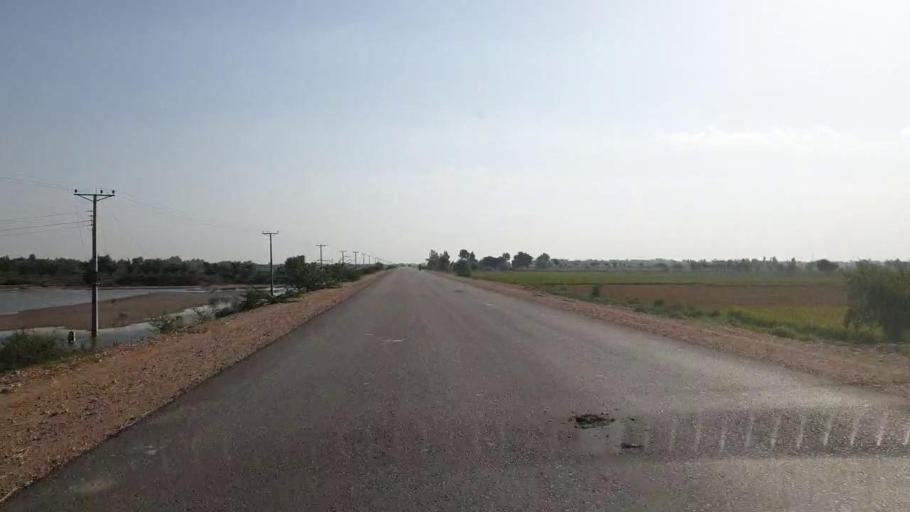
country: PK
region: Sindh
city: Tando Bago
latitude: 24.6571
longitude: 69.0080
